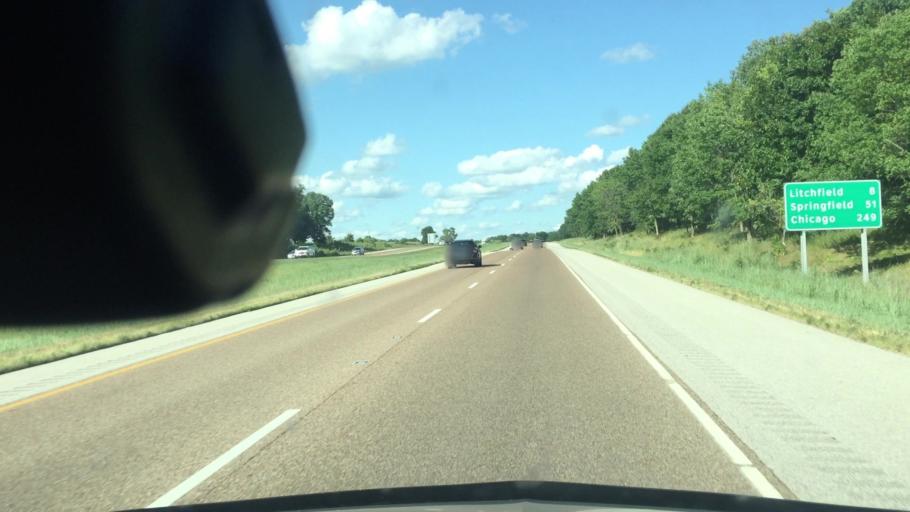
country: US
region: Illinois
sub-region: Macoupin County
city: Mount Olive
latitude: 39.0863
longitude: -89.7492
